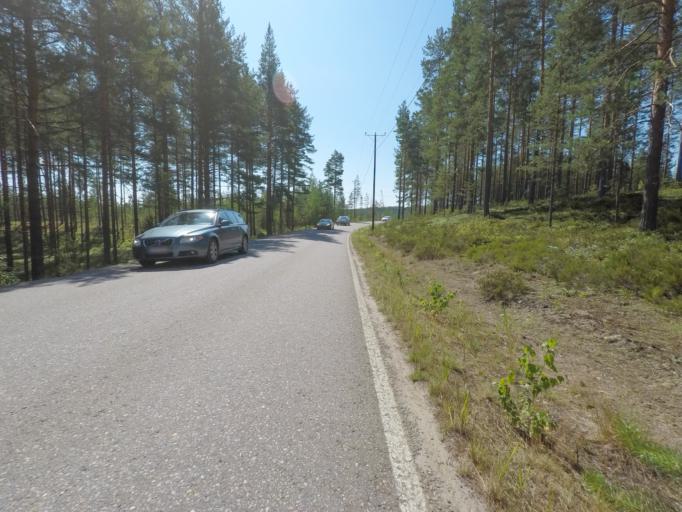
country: FI
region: Southern Savonia
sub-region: Mikkeli
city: Puumala
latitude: 61.4548
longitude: 28.1736
